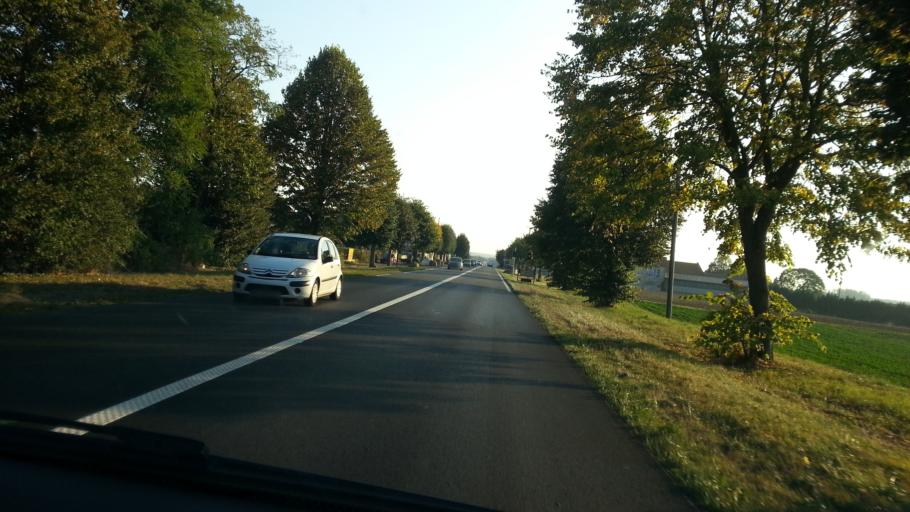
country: FR
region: Picardie
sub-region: Departement de l'Oise
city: Saint-Martin-Longueau
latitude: 49.3468
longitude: 2.6079
